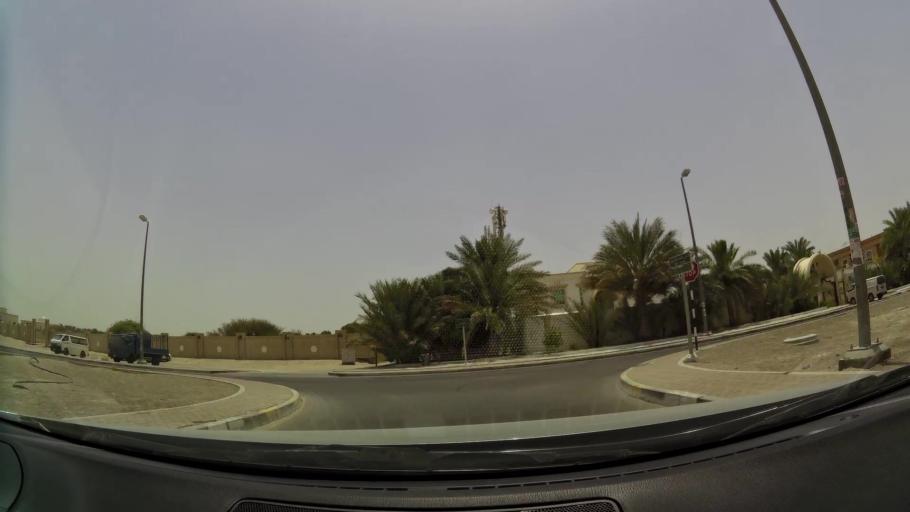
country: AE
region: Abu Dhabi
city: Al Ain
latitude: 24.1994
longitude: 55.7739
